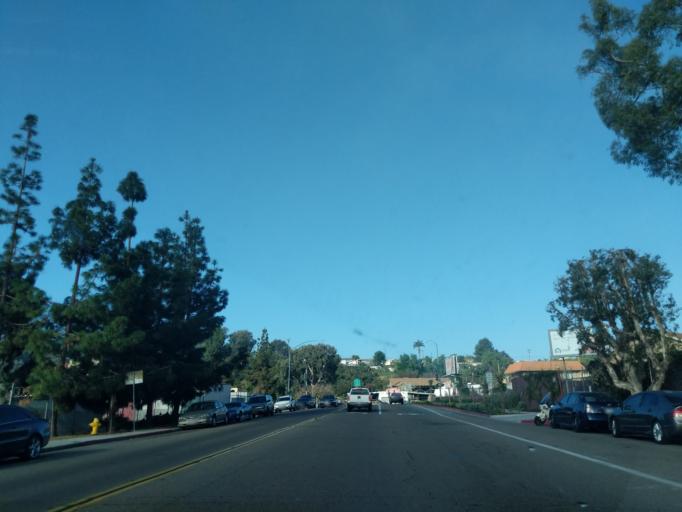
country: US
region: California
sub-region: San Diego County
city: National City
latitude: 32.7371
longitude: -117.0911
